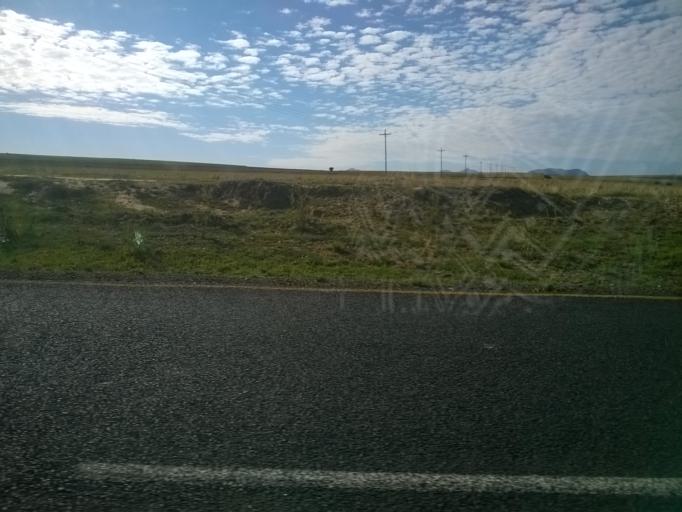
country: LS
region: Berea
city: Teyateyaneng
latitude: -29.1339
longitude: 27.7745
